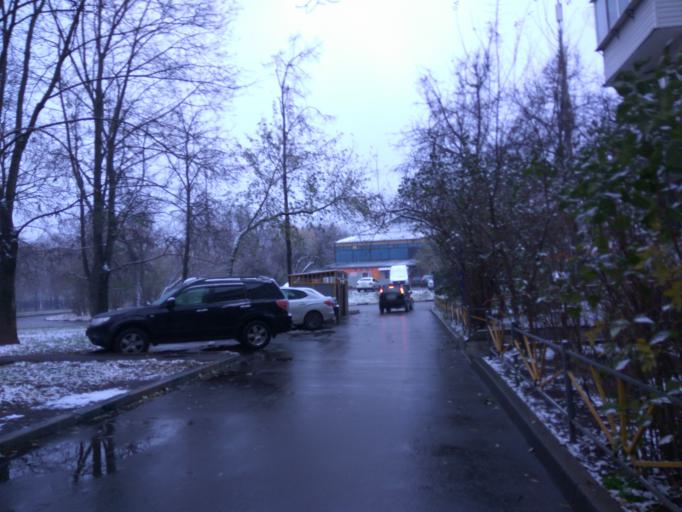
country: RU
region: Moscow
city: Orekhovo-Borisovo Severnoye
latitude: 55.6308
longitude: 37.6741
